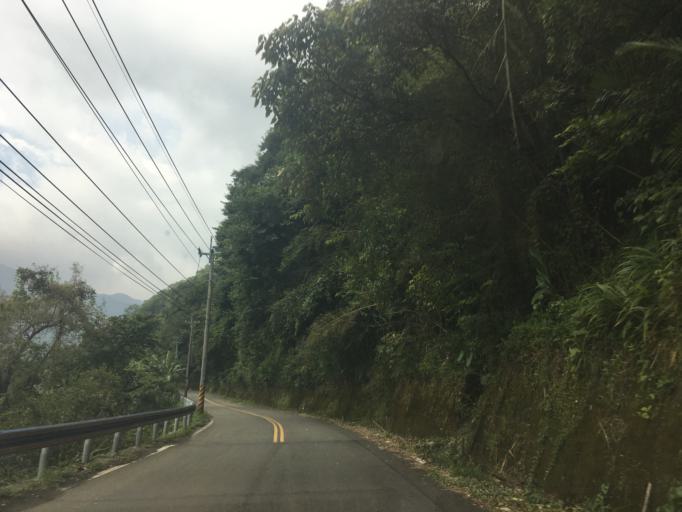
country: TW
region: Taiwan
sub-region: Miaoli
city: Miaoli
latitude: 24.3618
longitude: 120.9597
